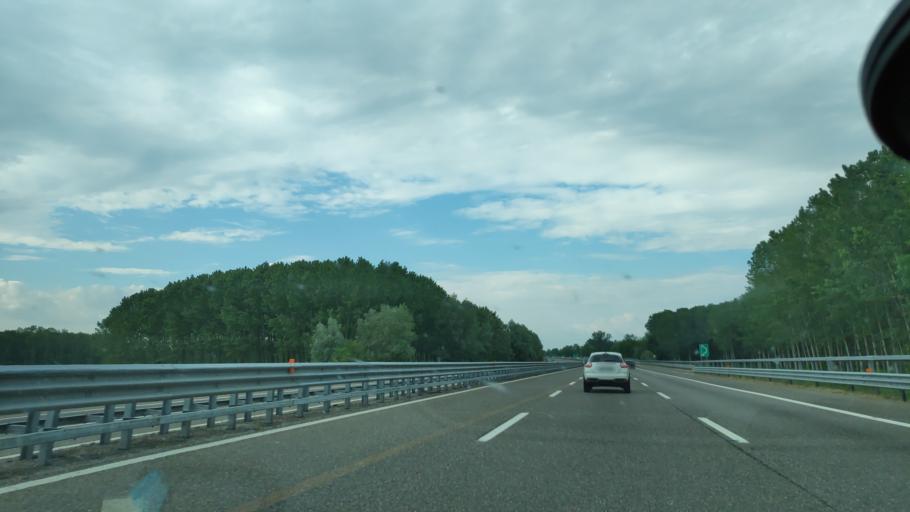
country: IT
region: Lombardy
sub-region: Provincia di Pavia
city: Pieve Albignola
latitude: 45.1087
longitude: 8.9739
